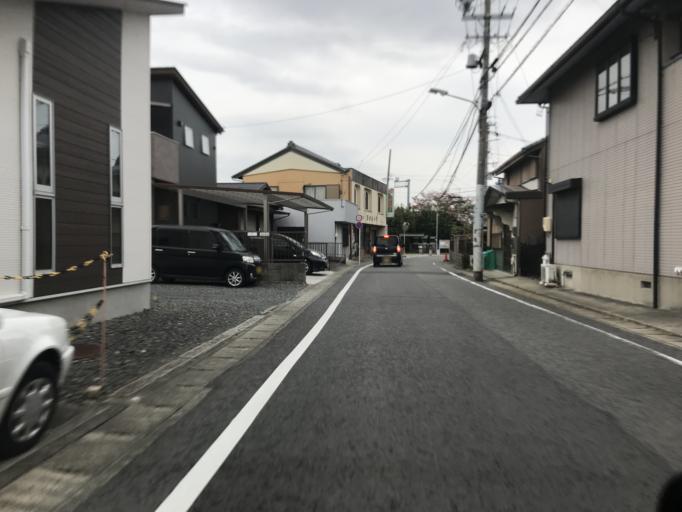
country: JP
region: Aichi
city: Inazawa
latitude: 35.2133
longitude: 136.8401
